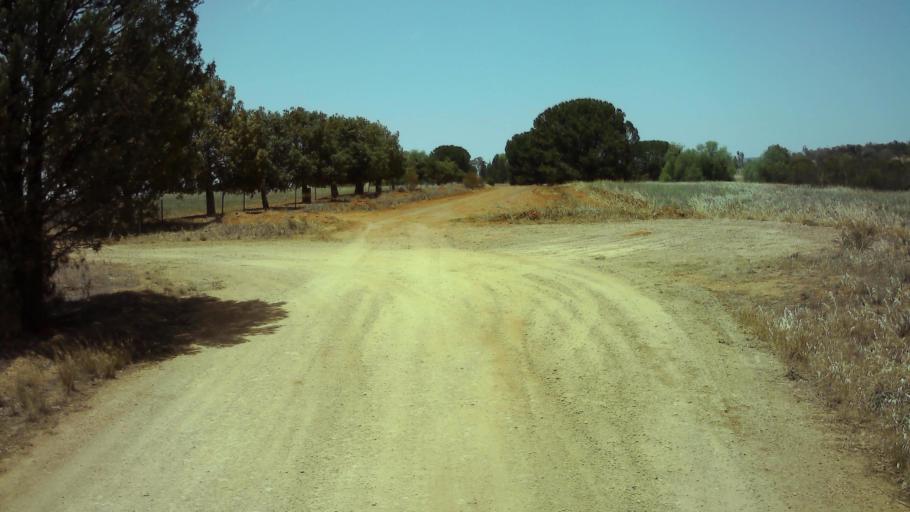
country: AU
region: New South Wales
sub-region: Weddin
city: Grenfell
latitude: -33.9114
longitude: 148.1649
